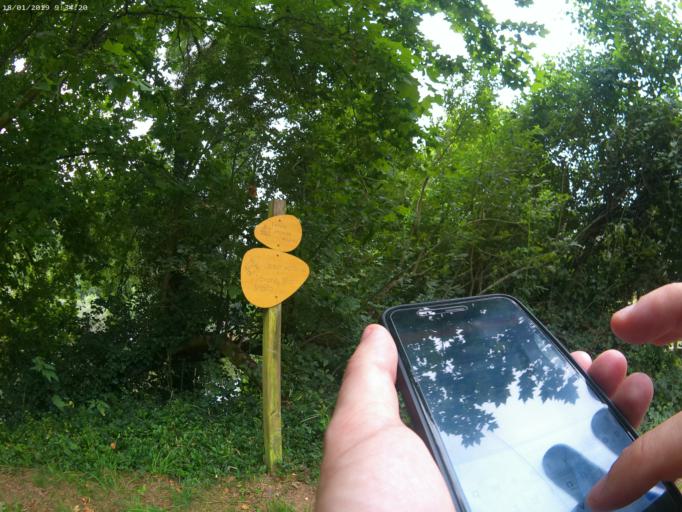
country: PT
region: Viana do Castelo
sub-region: Ponte da Barca
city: Ponte da Barca
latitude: 41.8018
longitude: -8.4735
